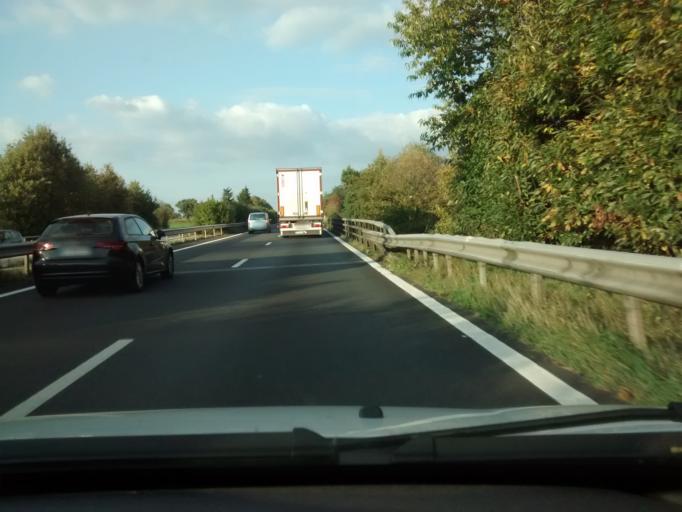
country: FR
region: Pays de la Loire
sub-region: Departement de la Loire-Atlantique
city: Nozay
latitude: 47.5775
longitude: -1.6297
